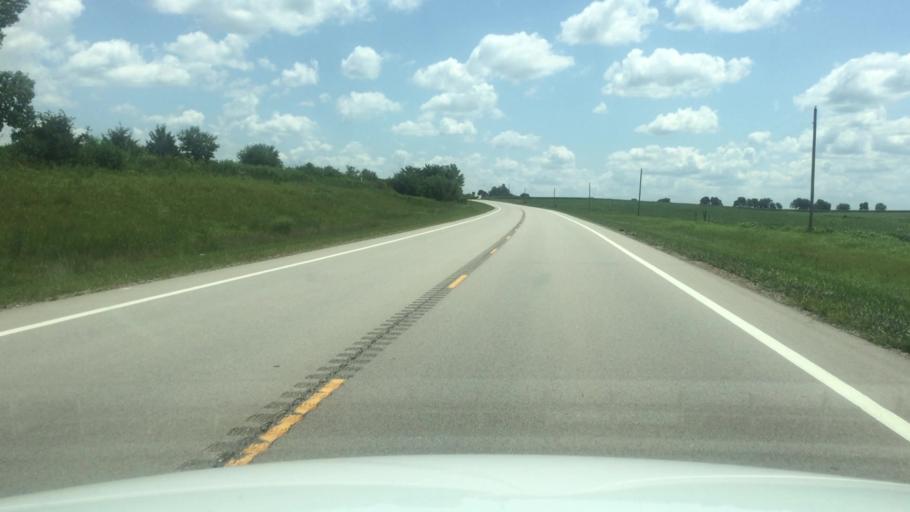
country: US
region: Kansas
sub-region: Brown County
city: Horton
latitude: 39.6139
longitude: -95.3470
